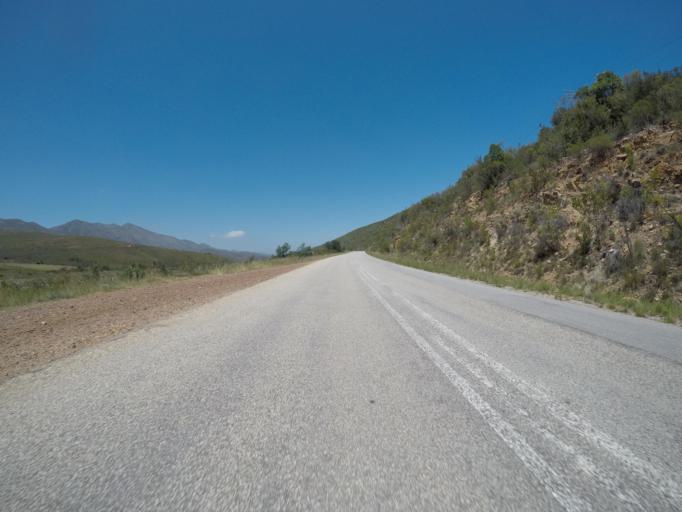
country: ZA
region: Eastern Cape
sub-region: Cacadu District Municipality
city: Kareedouw
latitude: -33.9032
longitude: 24.1346
